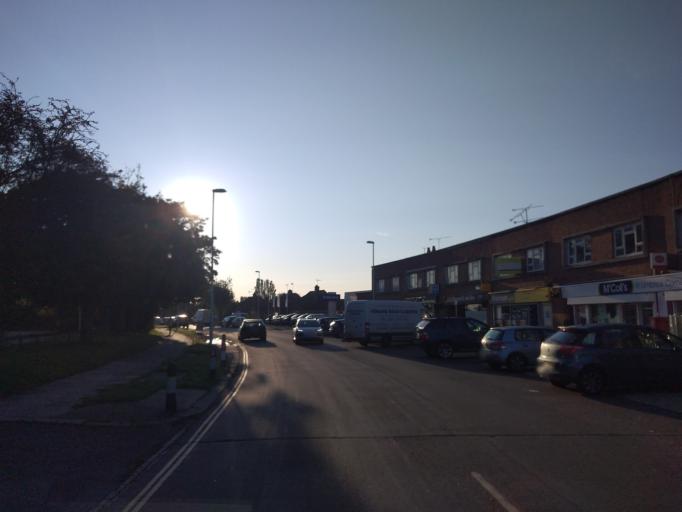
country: GB
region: England
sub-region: West Sussex
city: Goring-by-Sea
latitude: 50.8236
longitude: -0.4244
